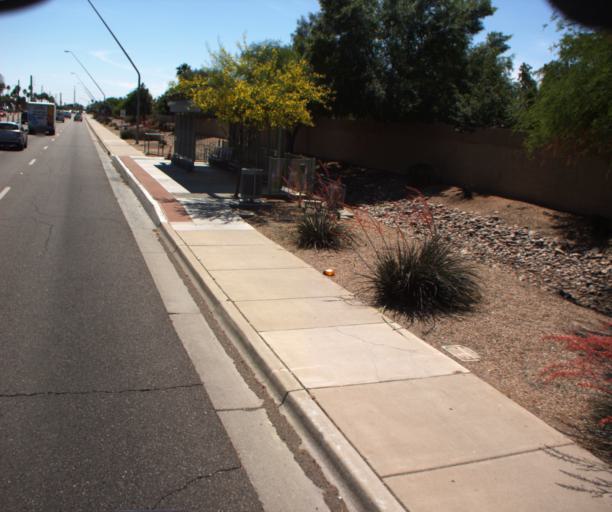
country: US
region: Arizona
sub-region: Maricopa County
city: San Carlos
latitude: 33.3683
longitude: -111.8421
